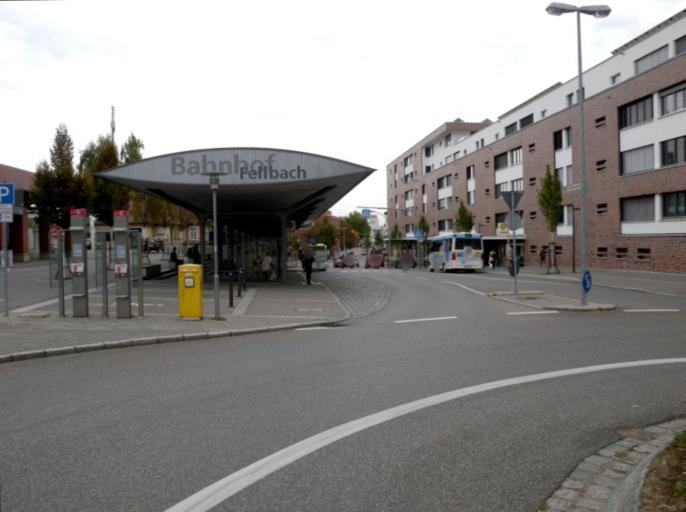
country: DE
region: Baden-Wuerttemberg
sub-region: Regierungsbezirk Stuttgart
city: Fellbach
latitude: 48.8197
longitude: 9.2702
